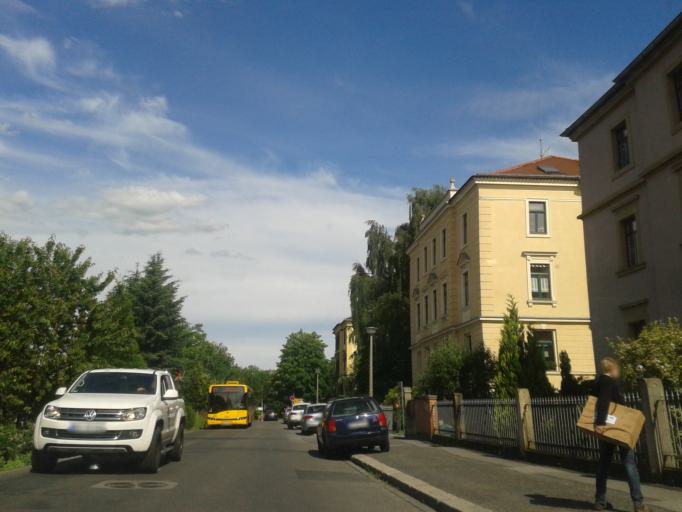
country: DE
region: Saxony
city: Dresden
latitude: 51.0157
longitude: 13.7696
